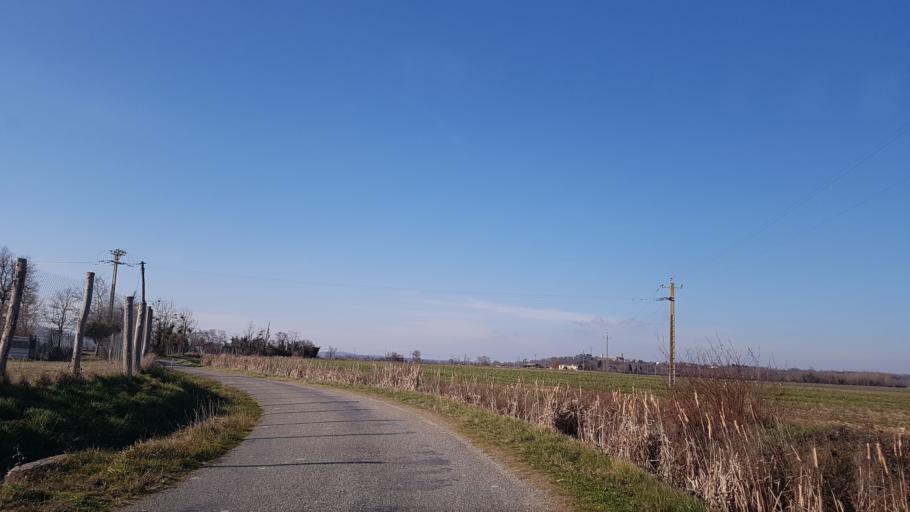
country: FR
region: Midi-Pyrenees
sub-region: Departement de l'Ariege
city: La Tour-du-Crieu
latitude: 43.1736
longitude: 1.6602
